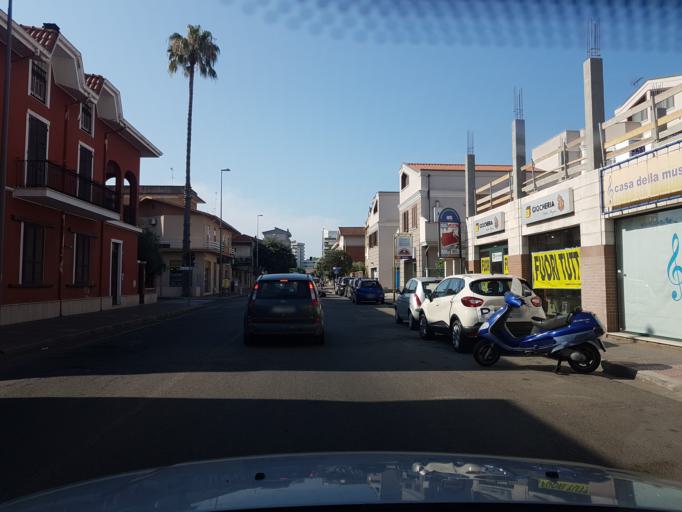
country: IT
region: Sardinia
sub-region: Provincia di Oristano
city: Oristano
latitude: 39.9060
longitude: 8.5884
